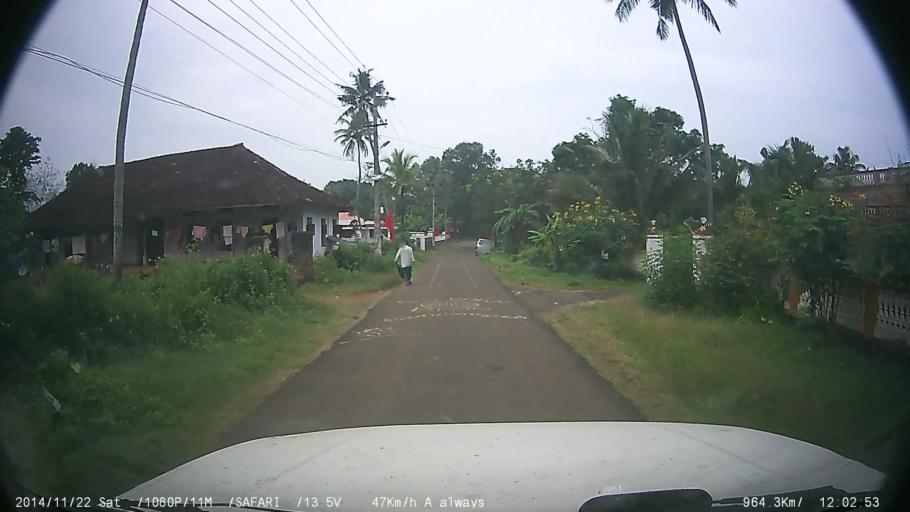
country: IN
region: Kerala
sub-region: Kottayam
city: Palackattumala
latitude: 9.7858
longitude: 76.5637
